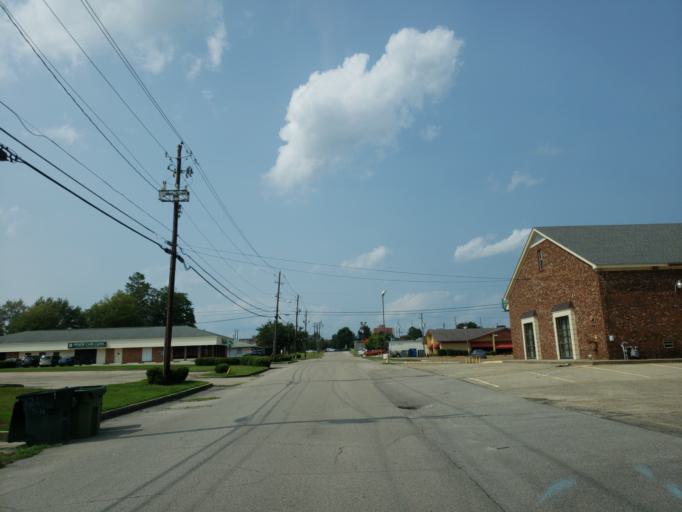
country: US
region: Mississippi
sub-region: Forrest County
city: Hattiesburg
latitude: 31.3223
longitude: -89.3301
